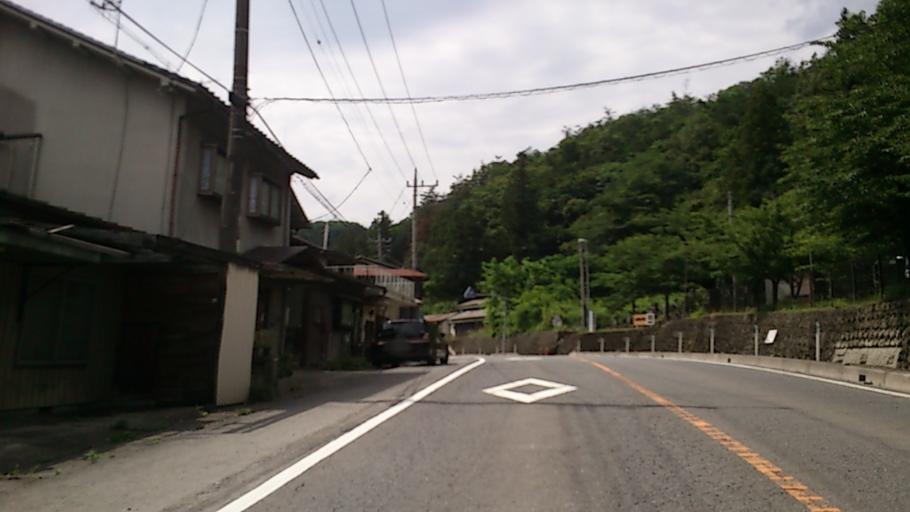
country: JP
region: Gunma
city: Tomioka
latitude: 36.2129
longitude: 138.7876
